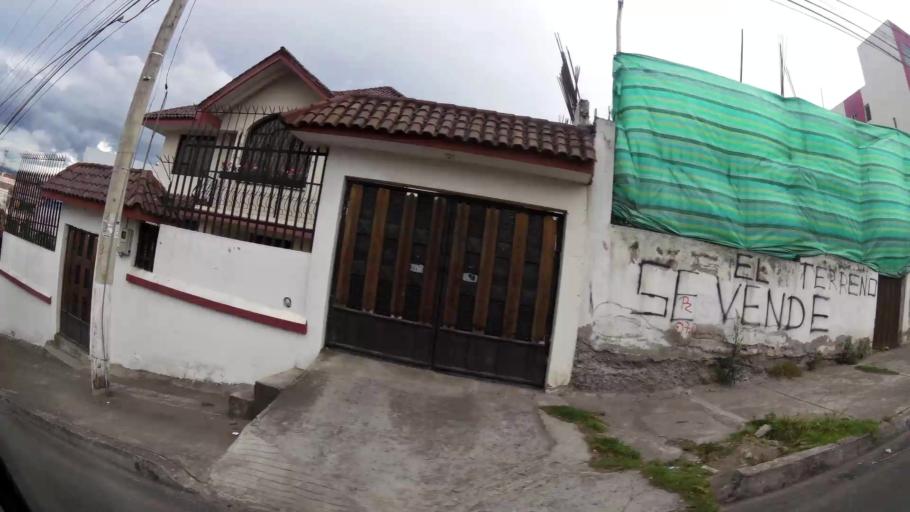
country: EC
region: Tungurahua
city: Ambato
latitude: -1.2715
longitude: -78.6308
